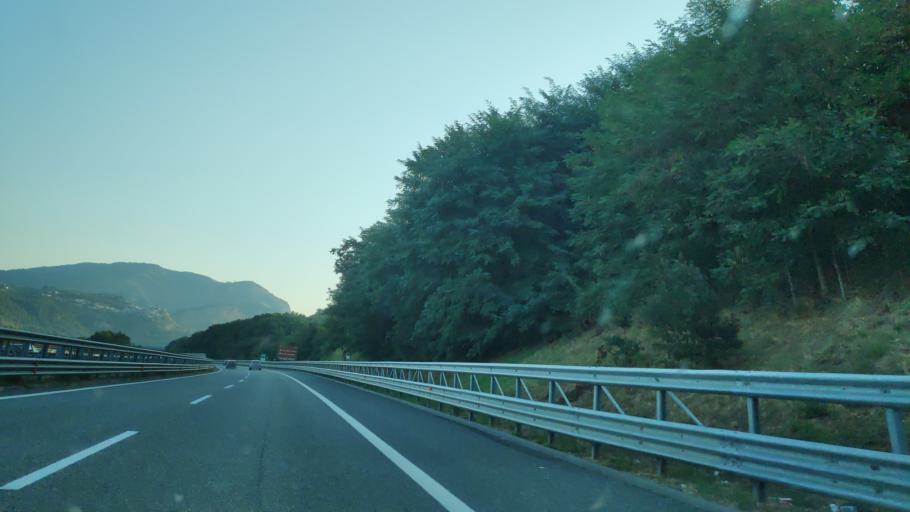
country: IT
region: Calabria
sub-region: Provincia di Catanzaro
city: Nocera Terinese
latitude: 39.0497
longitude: 16.1508
